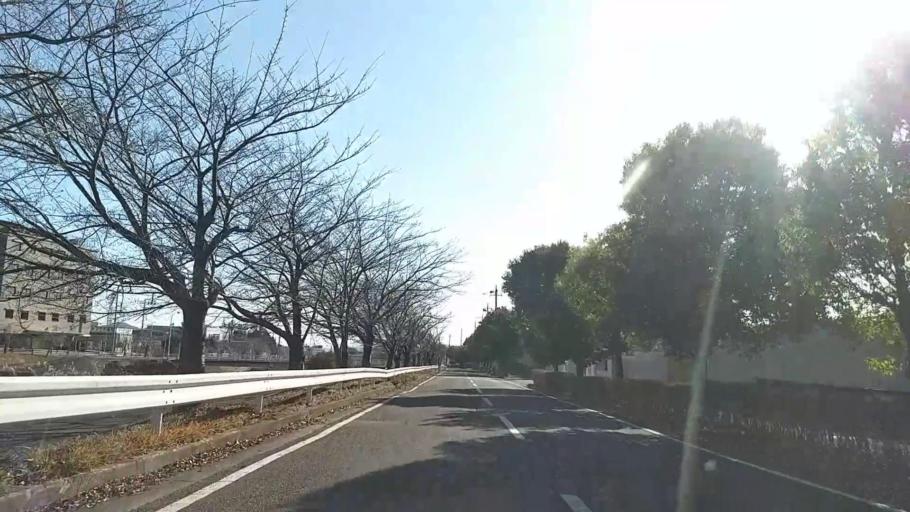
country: JP
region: Kanagawa
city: Hadano
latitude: 35.3855
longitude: 139.1928
